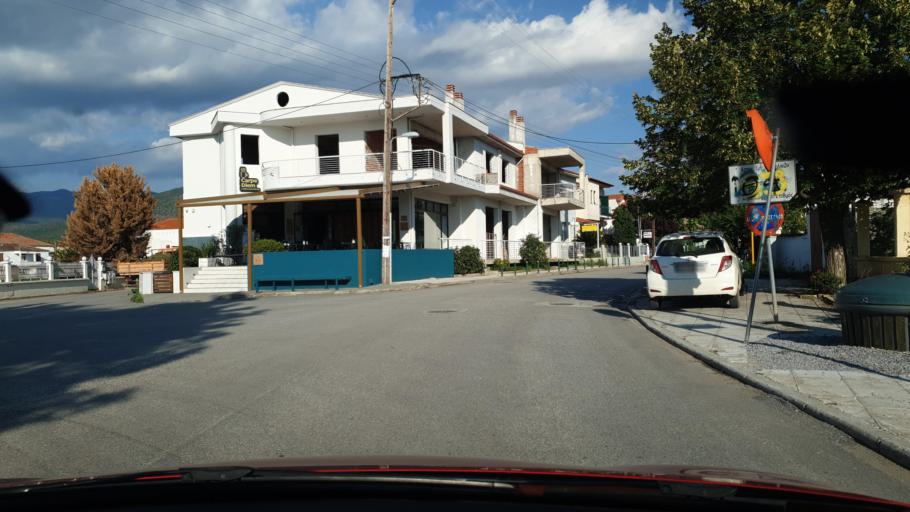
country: GR
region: Central Macedonia
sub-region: Nomos Thessalonikis
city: Vasilika
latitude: 40.4807
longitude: 23.1325
